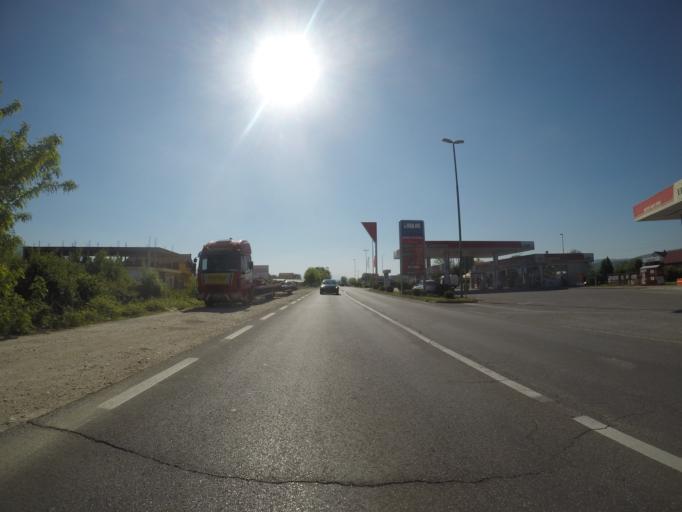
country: ME
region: Danilovgrad
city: Danilovgrad
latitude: 42.5450
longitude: 19.1038
